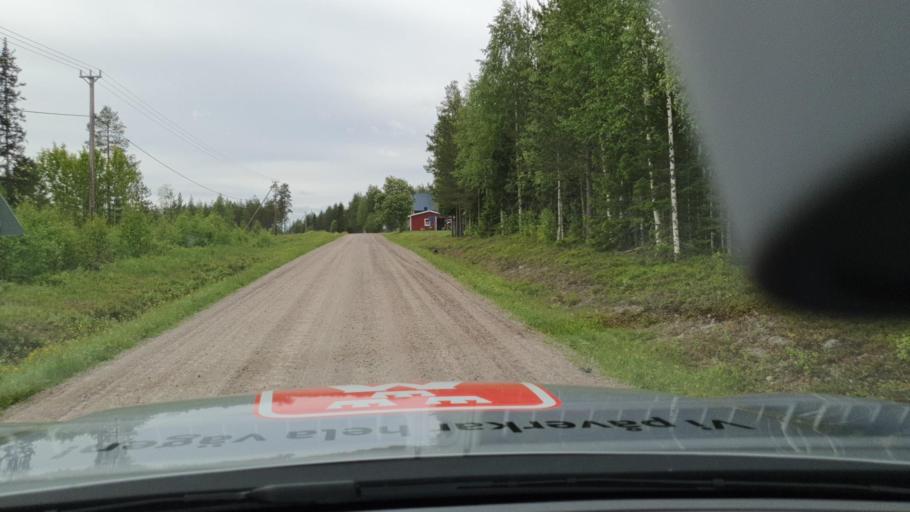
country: SE
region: Norrbotten
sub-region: Kalix Kommun
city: Kalix
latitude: 66.0309
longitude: 23.4392
